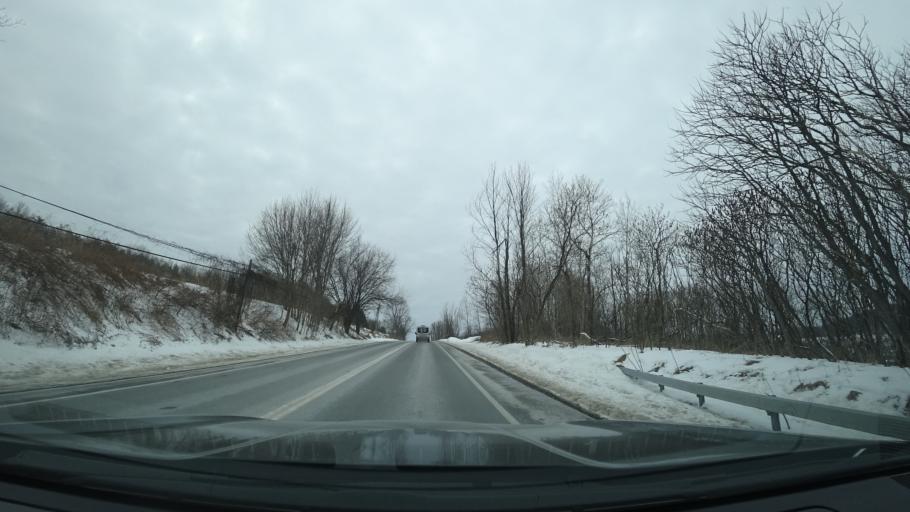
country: US
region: New York
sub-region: Washington County
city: Greenwich
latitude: 43.2041
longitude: -73.4861
